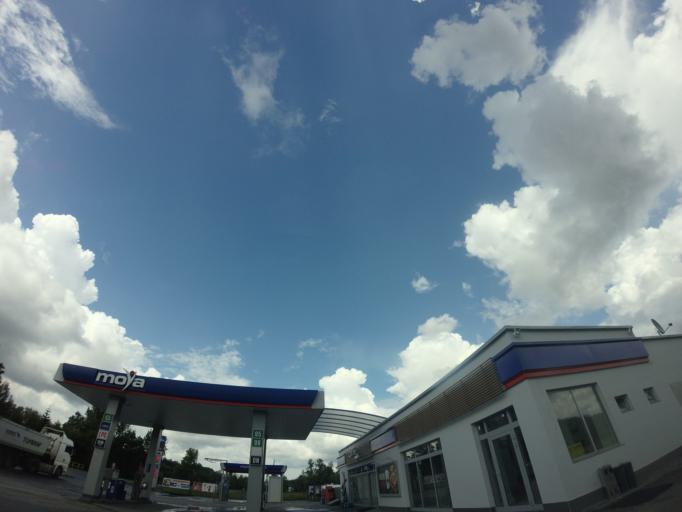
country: PL
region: Swietokrzyskie
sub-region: Powiat opatowski
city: Tarlow
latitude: 50.9866
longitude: 21.7133
